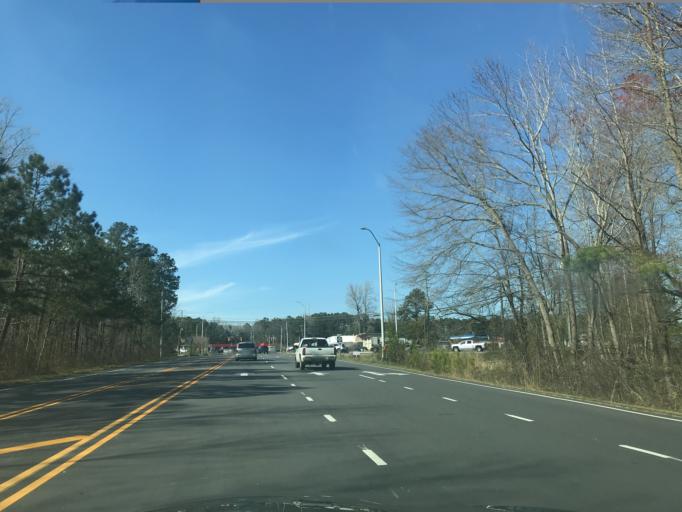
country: US
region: North Carolina
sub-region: Wake County
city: Fuquay-Varina
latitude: 35.5946
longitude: -78.7586
